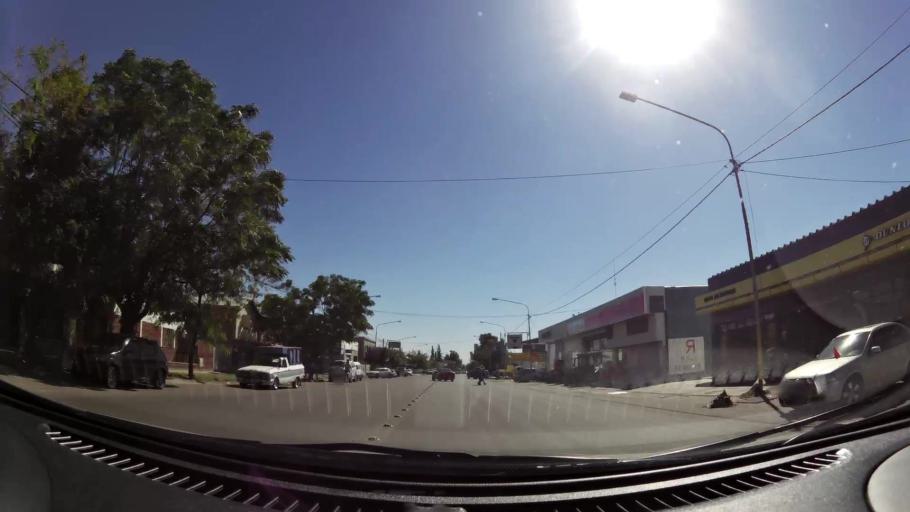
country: AR
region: Mendoza
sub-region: Departamento de Maipu
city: Maipu
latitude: -32.9484
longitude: -68.7865
